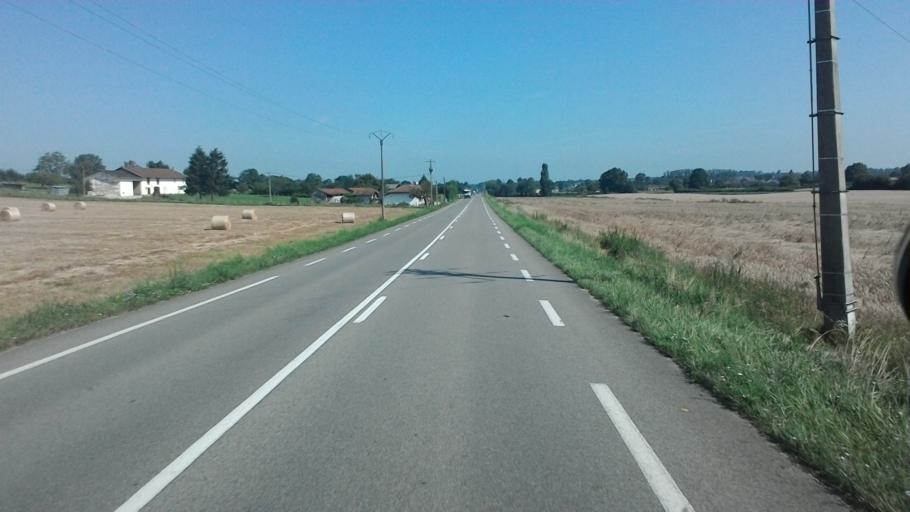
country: FR
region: Rhone-Alpes
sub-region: Departement de l'Ain
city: Montrevel-en-Bresse
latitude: 46.3820
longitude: 5.1168
